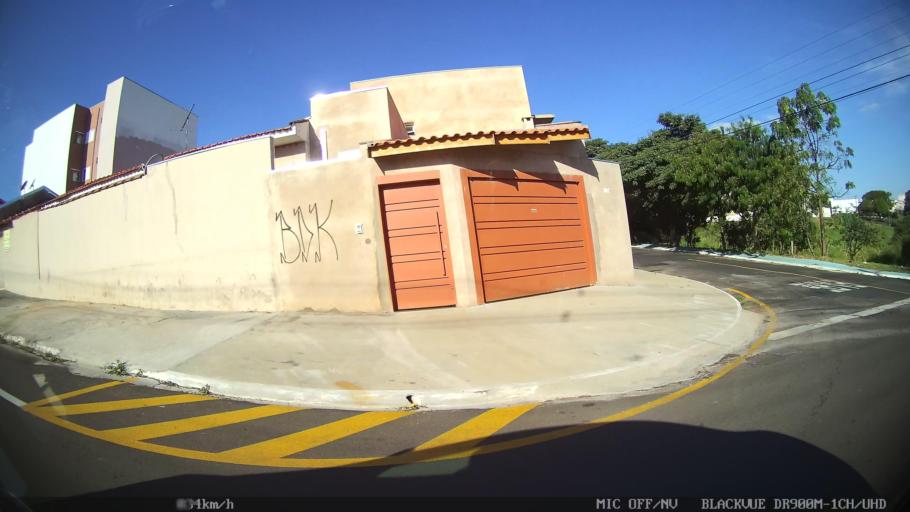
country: BR
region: Sao Paulo
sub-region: Franca
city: Franca
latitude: -20.5226
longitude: -47.4156
